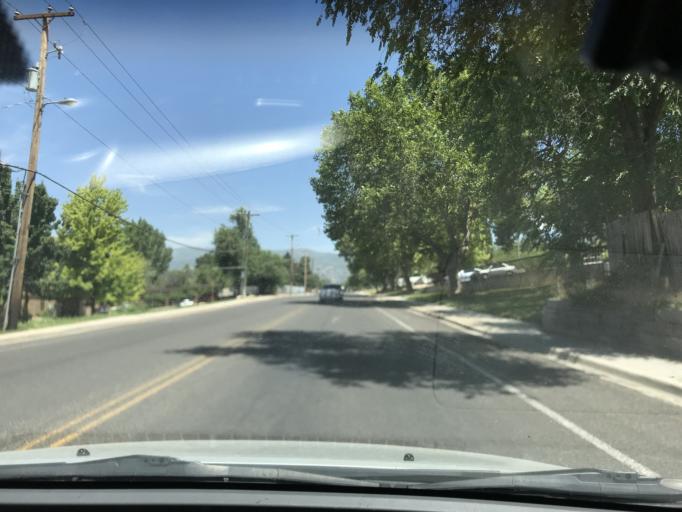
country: US
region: Utah
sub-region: Davis County
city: North Salt Lake
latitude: 40.8423
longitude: -111.9048
